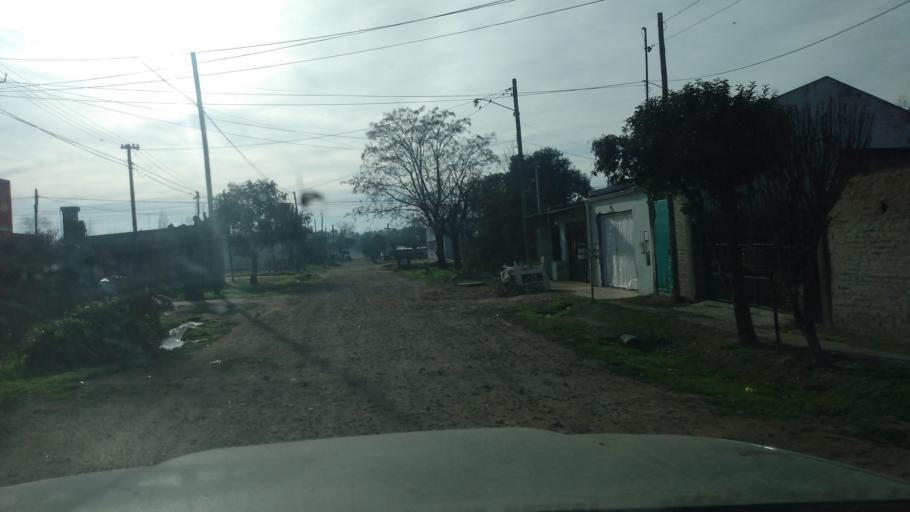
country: AR
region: Buenos Aires
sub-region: Partido de Lujan
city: Lujan
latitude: -34.5424
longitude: -59.1194
